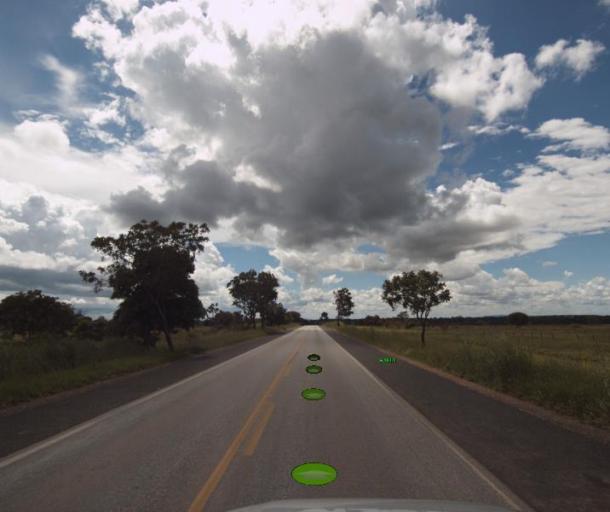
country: BR
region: Goias
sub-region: Uruacu
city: Uruacu
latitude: -14.0076
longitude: -49.0860
